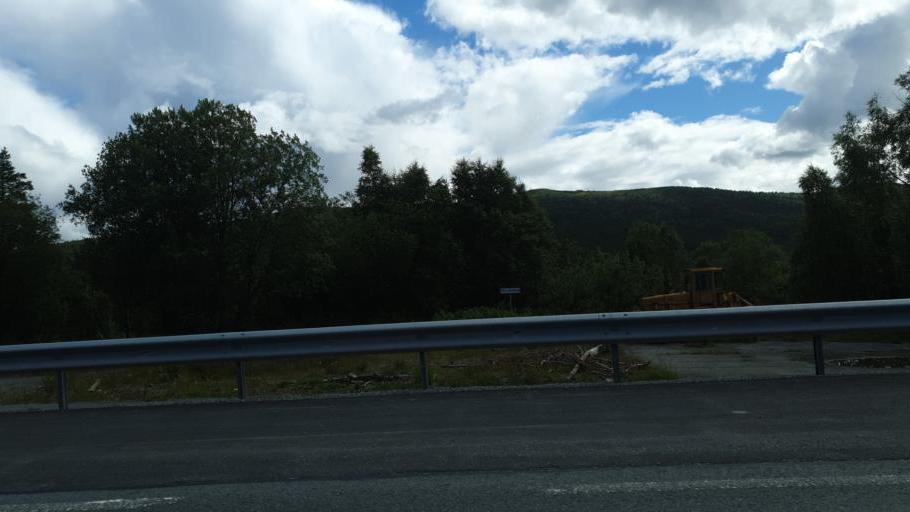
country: NO
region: Sor-Trondelag
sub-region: Rennebu
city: Berkak
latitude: 62.6802
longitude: 9.9244
